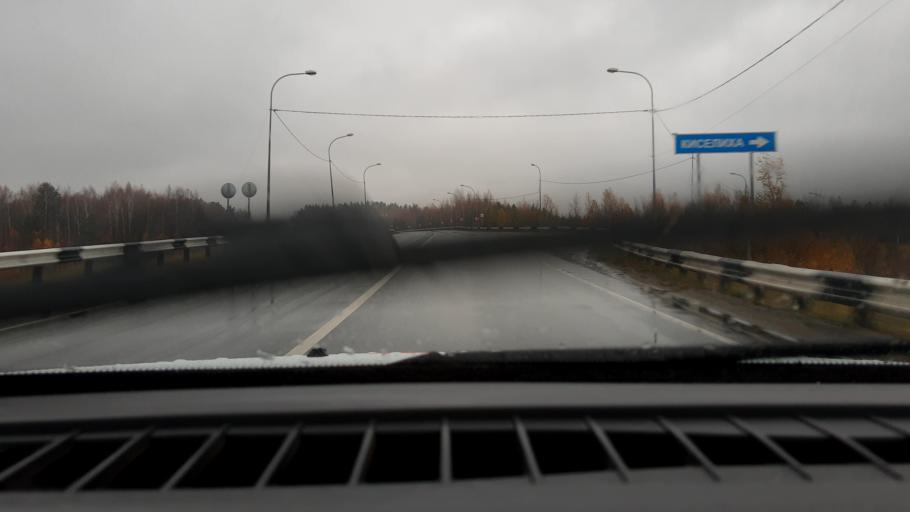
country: RU
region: Nizjnij Novgorod
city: Sitniki
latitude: 56.4691
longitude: 44.0366
